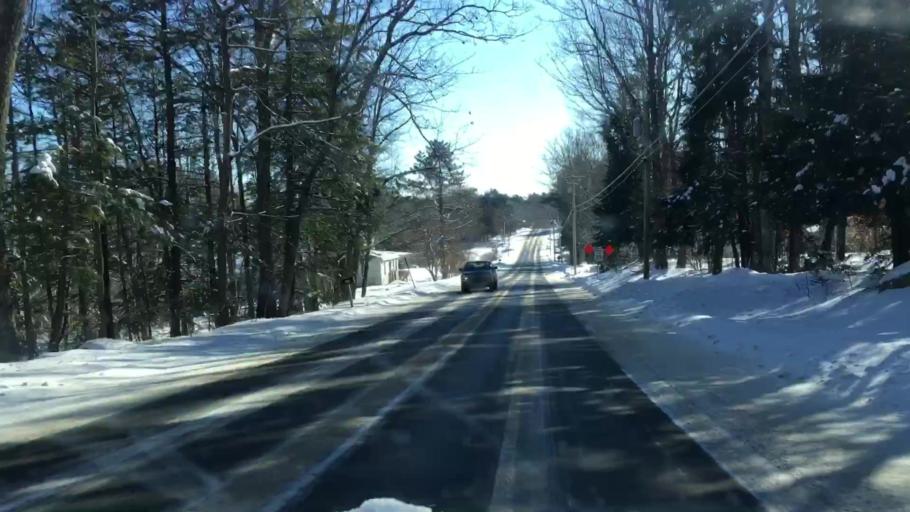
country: US
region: Maine
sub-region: Androscoggin County
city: Lisbon Falls
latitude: 43.9371
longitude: -70.0638
